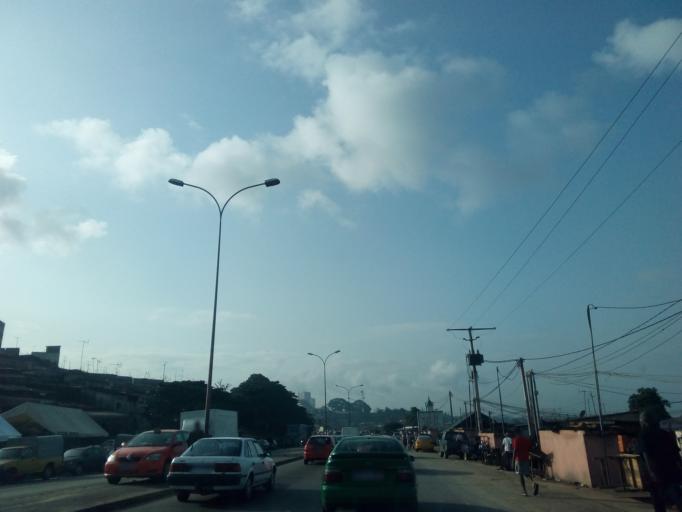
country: CI
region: Lagunes
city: Abidjan
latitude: 5.3434
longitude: -4.0369
